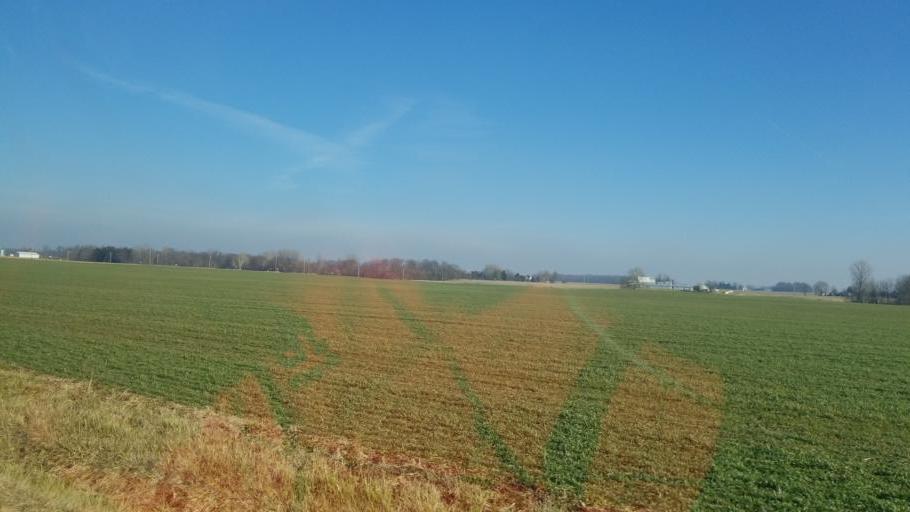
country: US
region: Ohio
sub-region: Crawford County
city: Bucyrus
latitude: 40.9468
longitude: -83.0742
